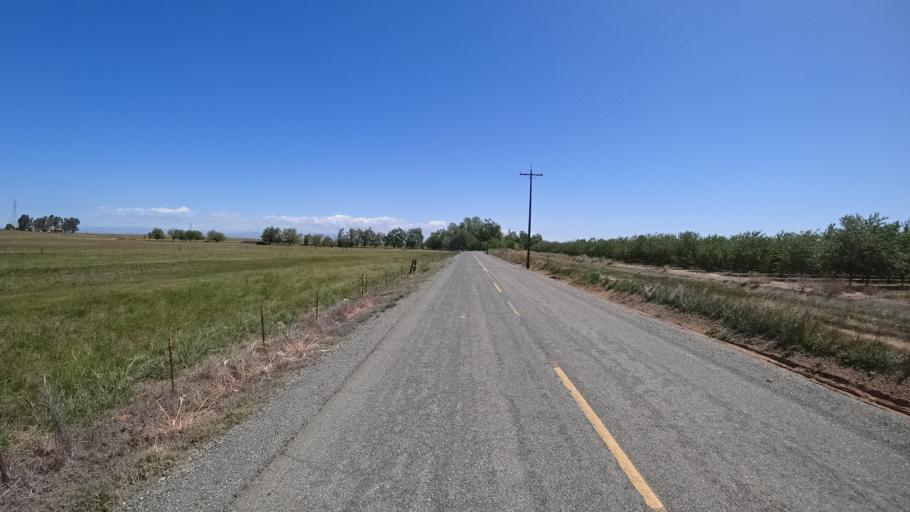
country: US
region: California
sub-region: Glenn County
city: Orland
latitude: 39.7951
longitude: -122.2334
